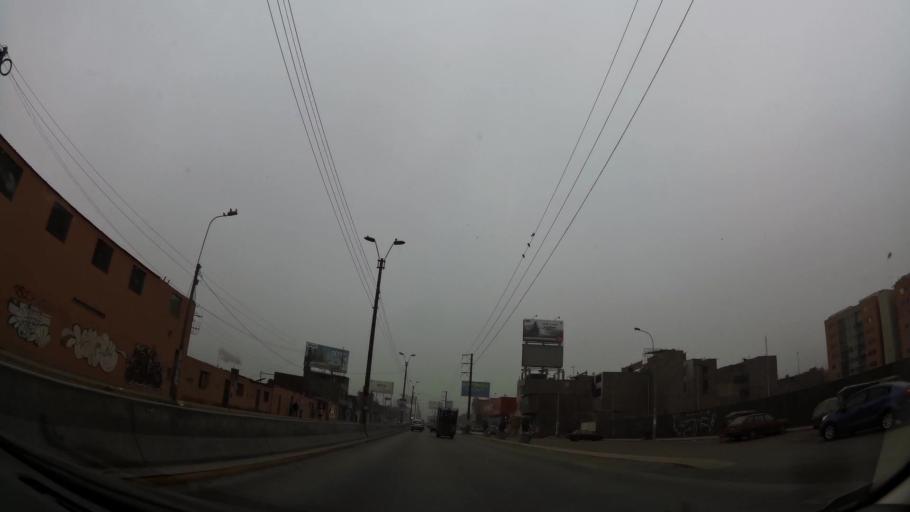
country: PE
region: Lima
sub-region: Lima
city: Santa Maria
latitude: -12.0160
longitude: -76.8892
